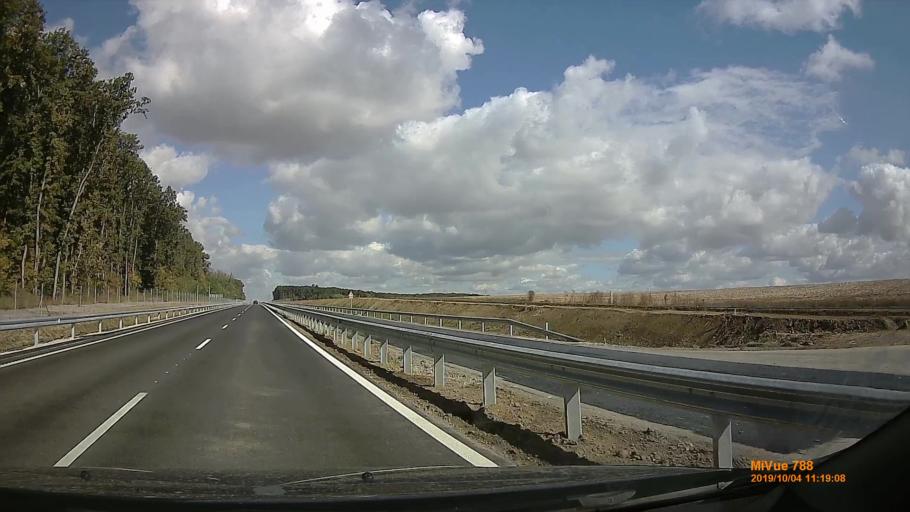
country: HU
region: Somogy
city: Kaposvar
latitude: 46.4787
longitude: 17.8043
